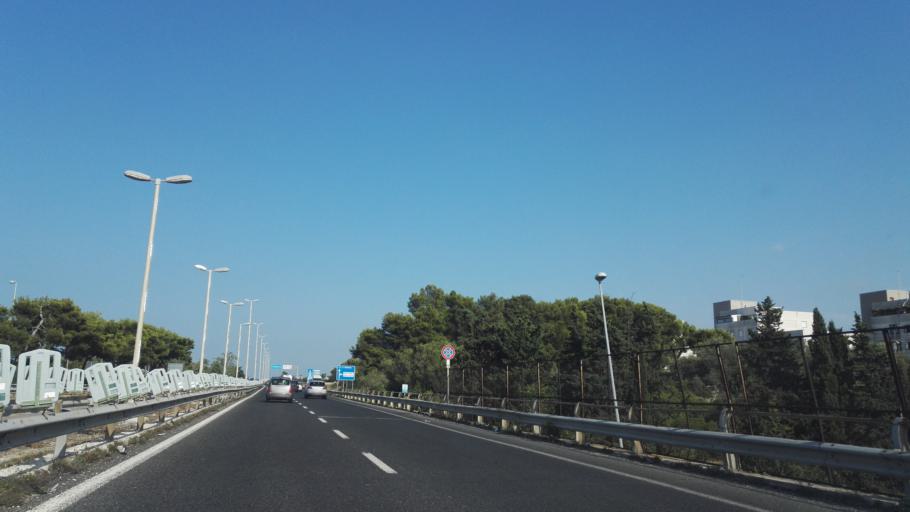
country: IT
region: Apulia
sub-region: Provincia di Bari
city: Parco Scizzo-Parchitello
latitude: 41.0834
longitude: 16.9992
